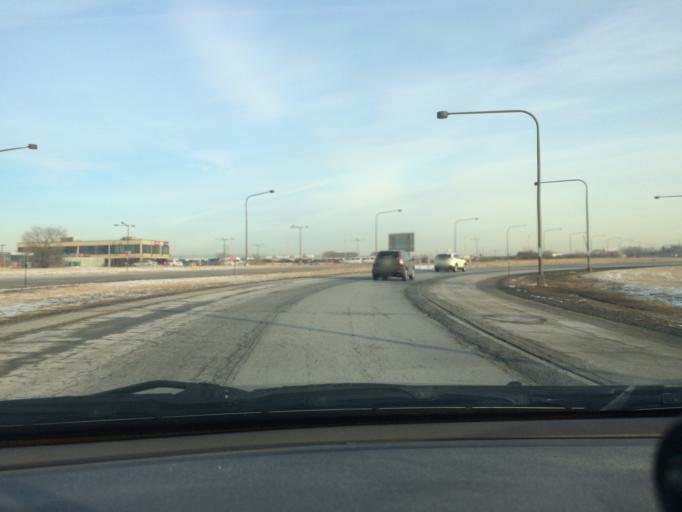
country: US
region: Illinois
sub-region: Cook County
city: Rosemont
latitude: 41.9813
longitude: -87.8810
